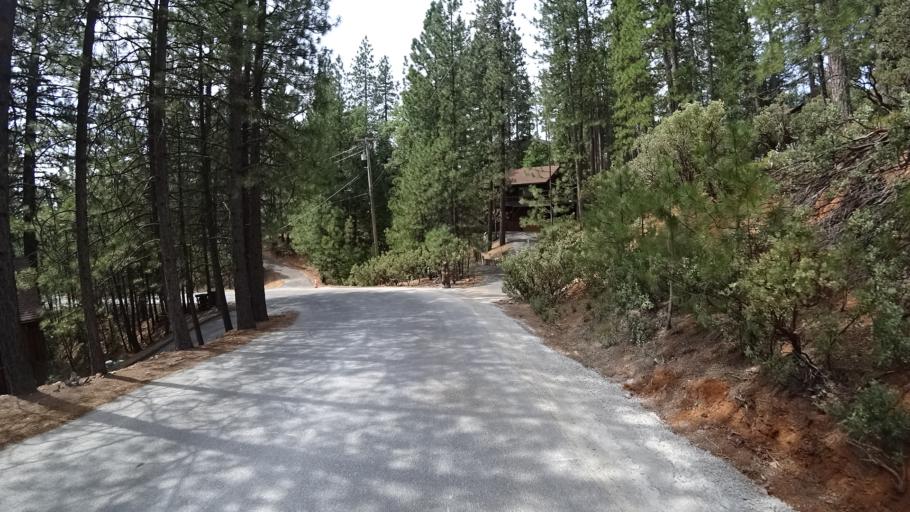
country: US
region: California
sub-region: Calaveras County
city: Arnold
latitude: 38.2440
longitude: -120.3456
